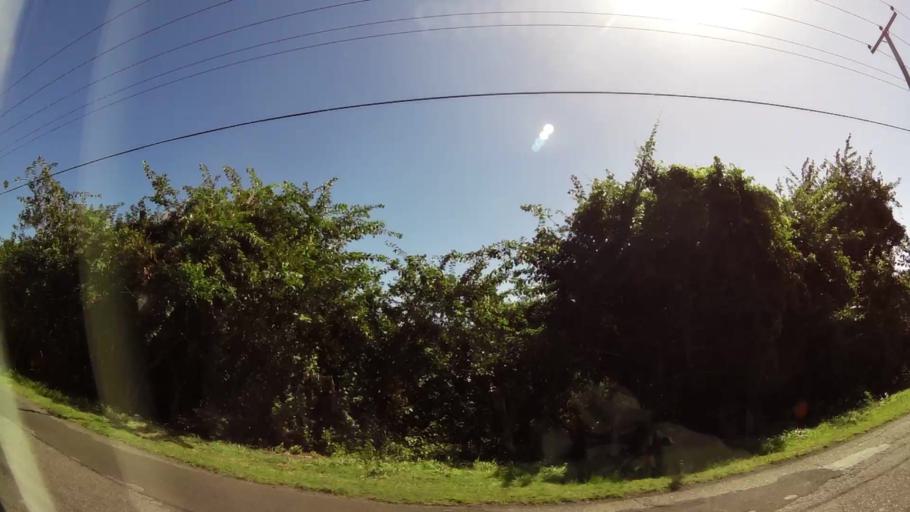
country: LC
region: Vieux-Fort
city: Vieux Fort
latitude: 13.7442
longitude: -60.9531
